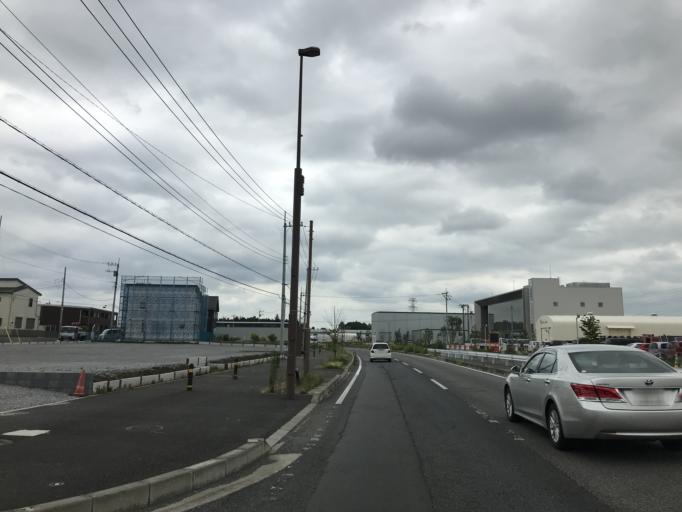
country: JP
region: Ibaraki
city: Ushiku
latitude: 36.0120
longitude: 140.0680
